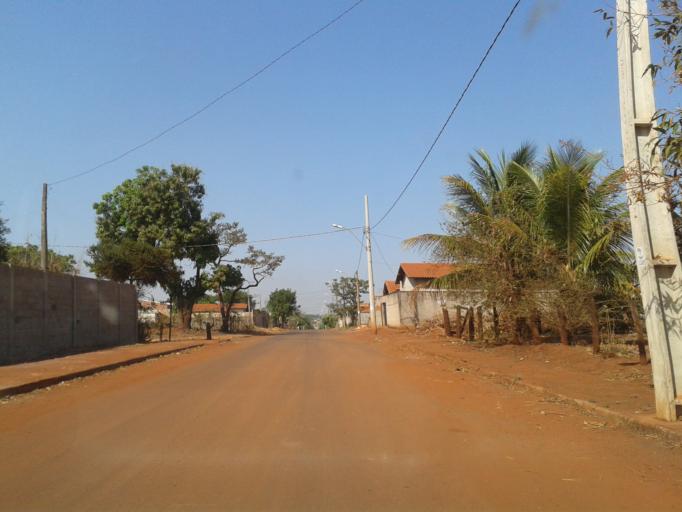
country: BR
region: Minas Gerais
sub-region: Ituiutaba
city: Ituiutaba
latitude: -18.9575
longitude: -49.4824
